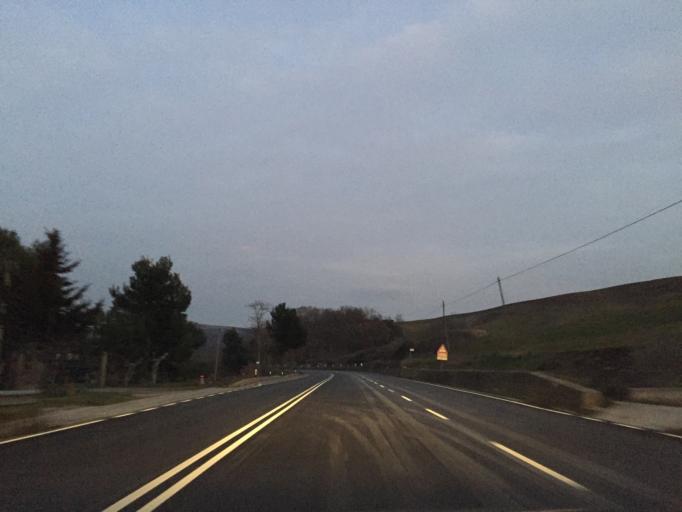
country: IT
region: Apulia
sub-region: Provincia di Foggia
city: Volturara Appula
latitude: 41.4561
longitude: 15.0667
